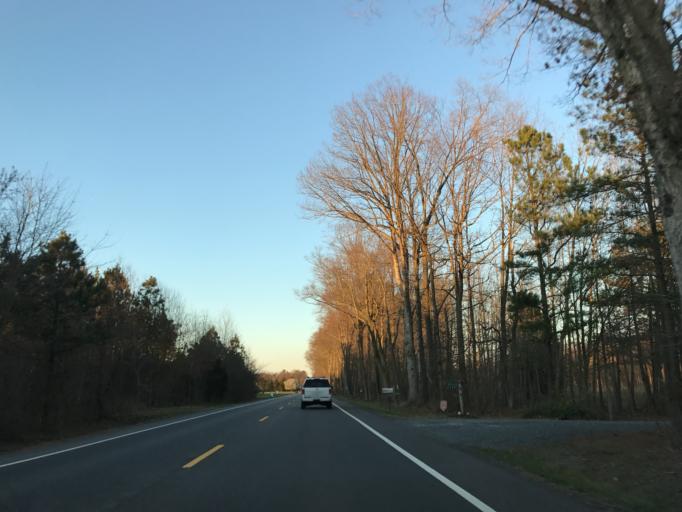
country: US
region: Maryland
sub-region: Talbot County
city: Easton
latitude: 38.8324
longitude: -76.0319
